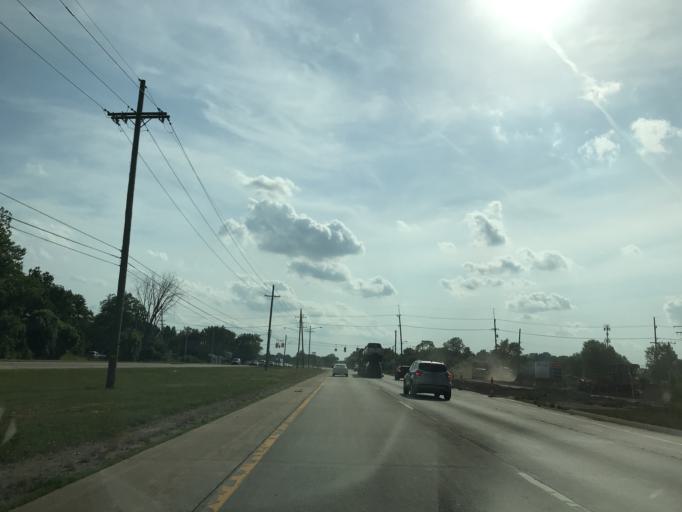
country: US
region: Michigan
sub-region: Wayne County
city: Canton
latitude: 42.2623
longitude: -83.5222
